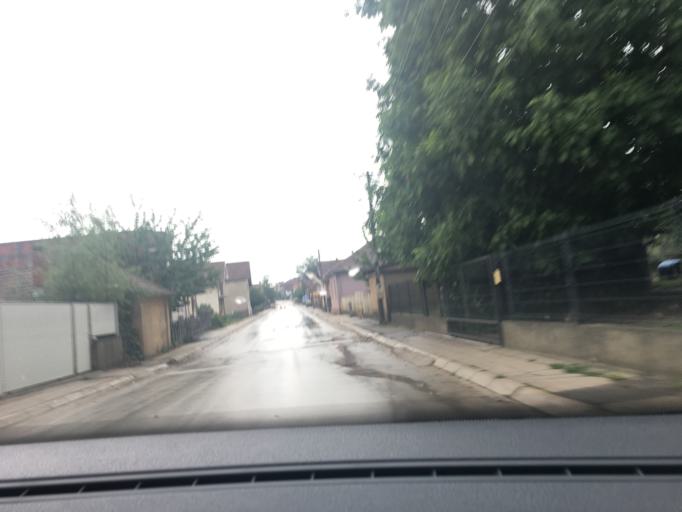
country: RS
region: Central Serbia
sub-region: Nisavski Okrug
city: Aleksinac
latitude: 43.5474
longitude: 21.7063
